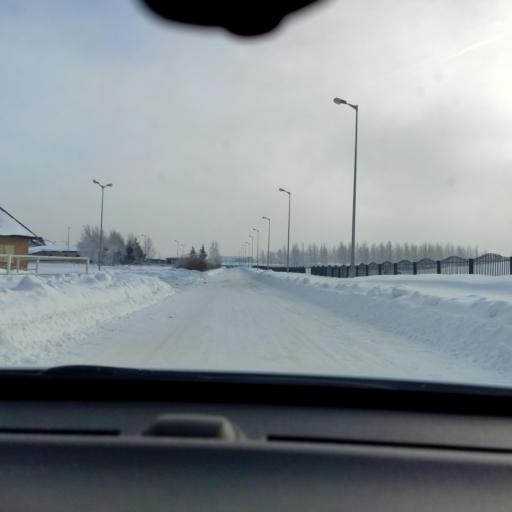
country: RU
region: Tatarstan
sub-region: Gorod Kazan'
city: Kazan
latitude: 55.7916
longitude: 49.2009
